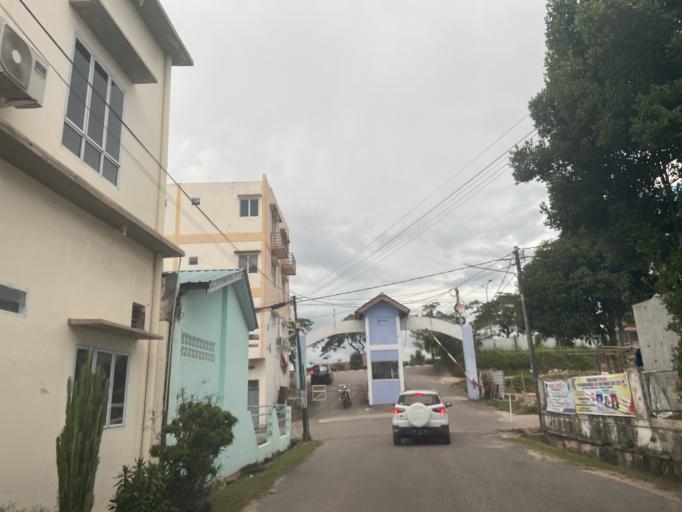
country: SG
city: Singapore
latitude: 1.1242
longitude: 104.0223
